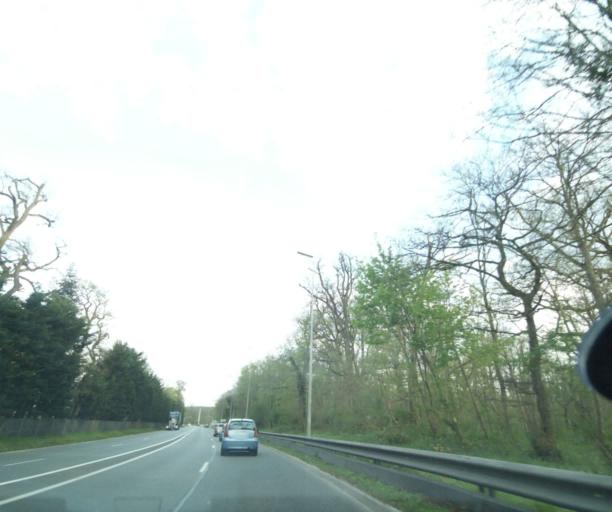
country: FR
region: Ile-de-France
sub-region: Departement de Seine-et-Marne
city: Fontainebleau
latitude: 48.4002
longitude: 2.6877
